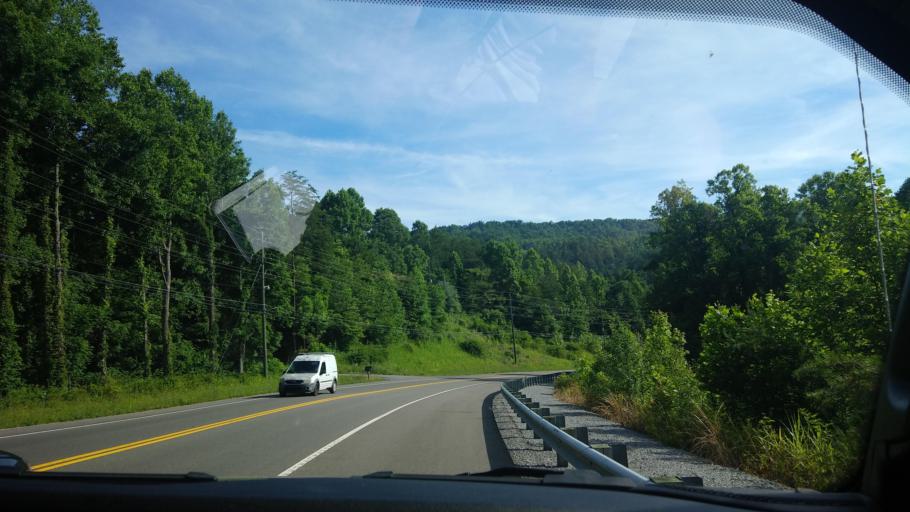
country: US
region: Tennessee
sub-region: Sevier County
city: Gatlinburg
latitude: 35.7562
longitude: -83.3849
